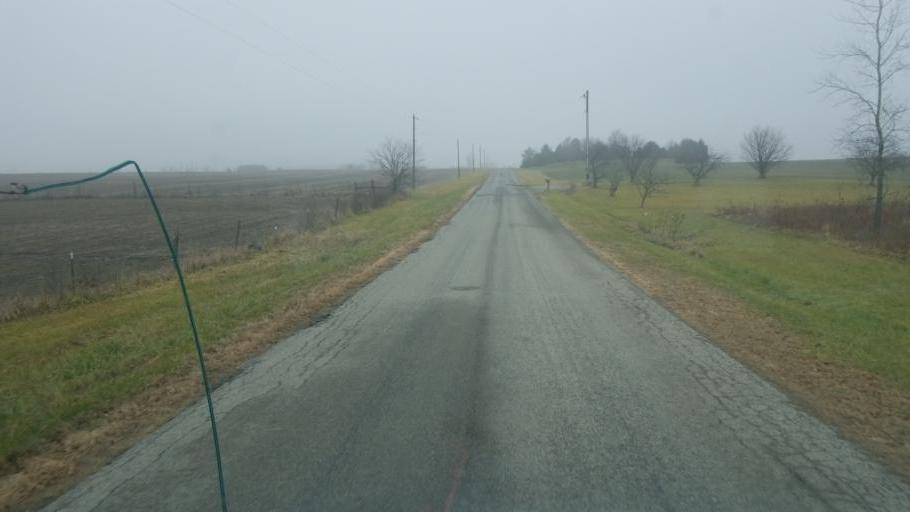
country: US
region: Ohio
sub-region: Champaign County
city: North Lewisburg
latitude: 40.3740
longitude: -83.5259
